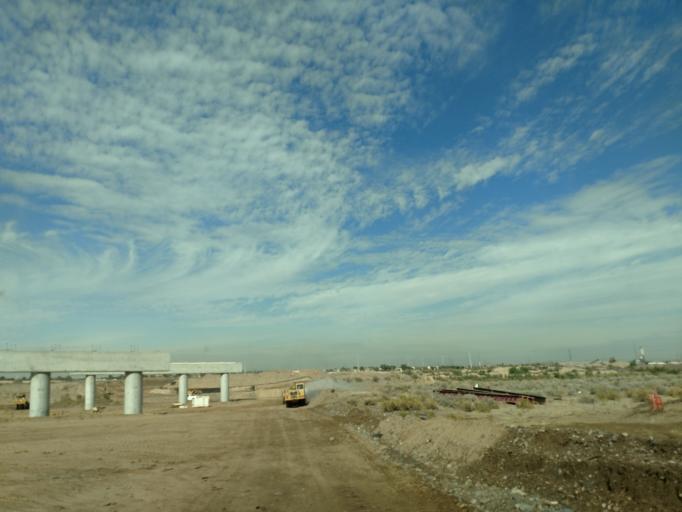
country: US
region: Arizona
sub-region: Maricopa County
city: Laveen
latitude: 33.3990
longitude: -112.1916
